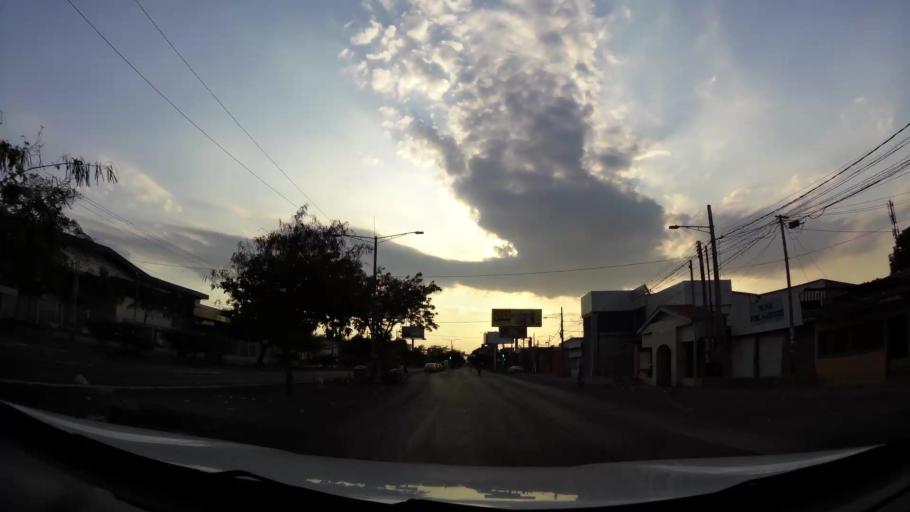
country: NI
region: Managua
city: Managua
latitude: 12.1519
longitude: -86.2379
